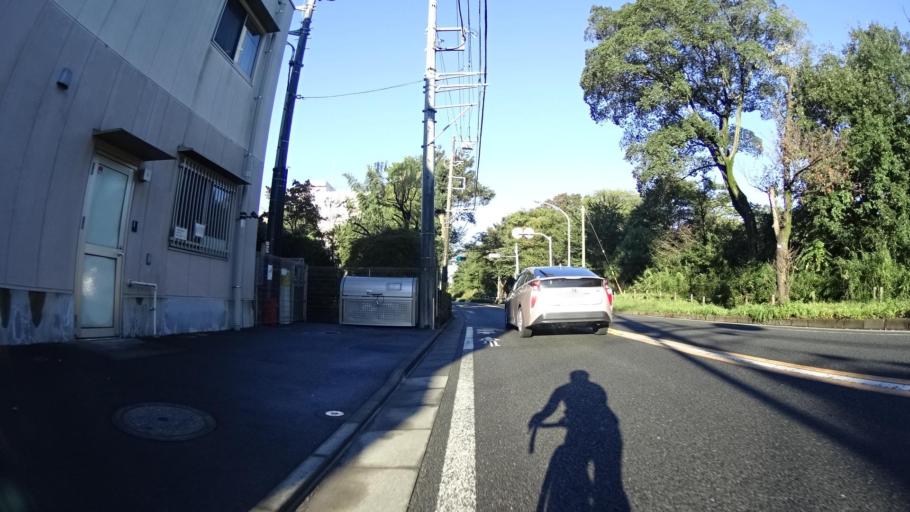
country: JP
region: Tokyo
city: Kokubunji
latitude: 35.7172
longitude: 139.4769
